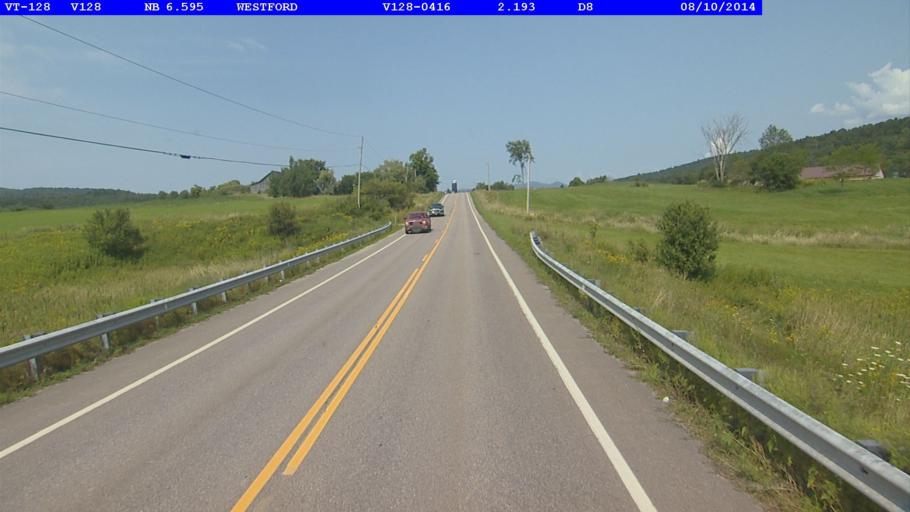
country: US
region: Vermont
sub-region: Chittenden County
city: Jericho
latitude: 44.5892
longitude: -73.0144
